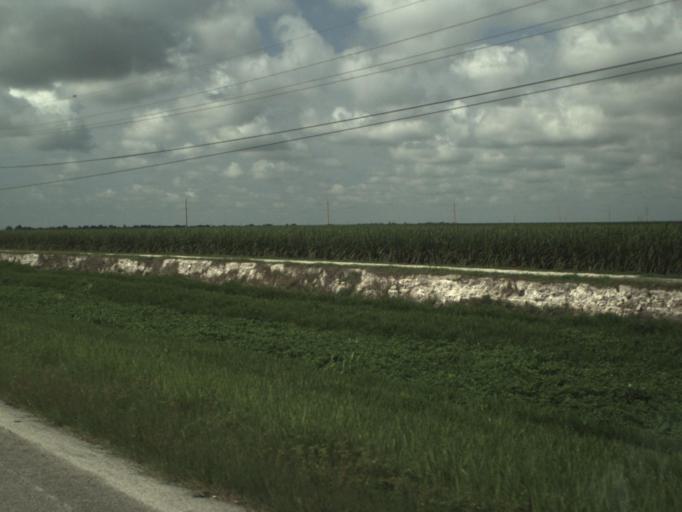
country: US
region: Florida
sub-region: Palm Beach County
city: Belle Glade
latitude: 26.7311
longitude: -80.6841
